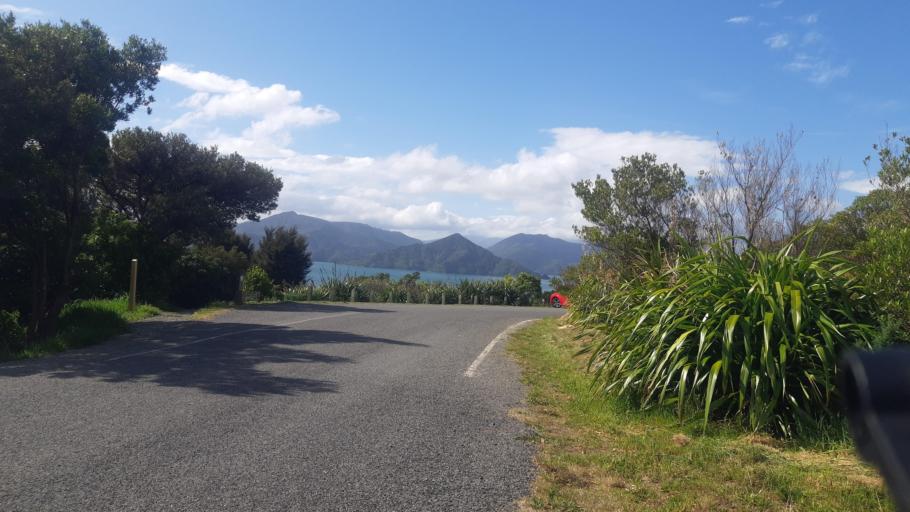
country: NZ
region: Marlborough
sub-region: Marlborough District
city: Picton
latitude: -41.2750
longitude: 174.0191
